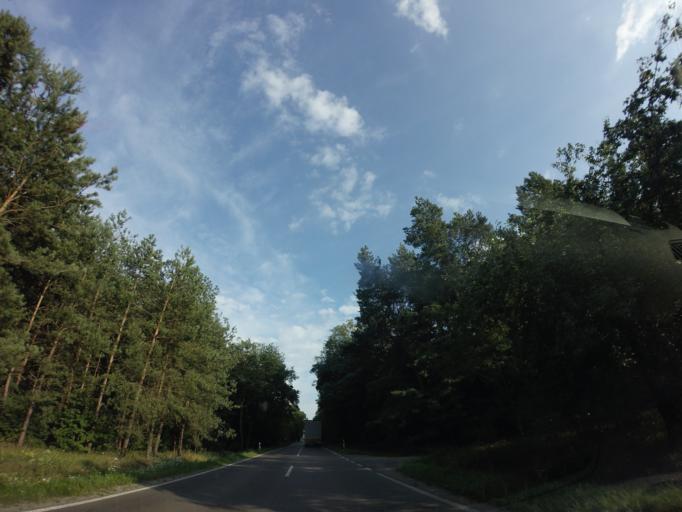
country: PL
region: Lublin Voivodeship
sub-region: Powiat lubartowski
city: Michow
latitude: 51.5377
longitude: 22.3082
